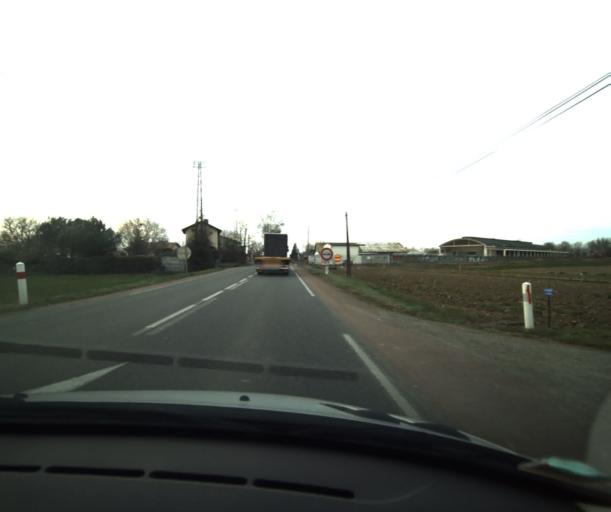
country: FR
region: Midi-Pyrenees
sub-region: Departement du Tarn-et-Garonne
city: Saint-Porquier
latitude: 44.0255
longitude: 1.1455
